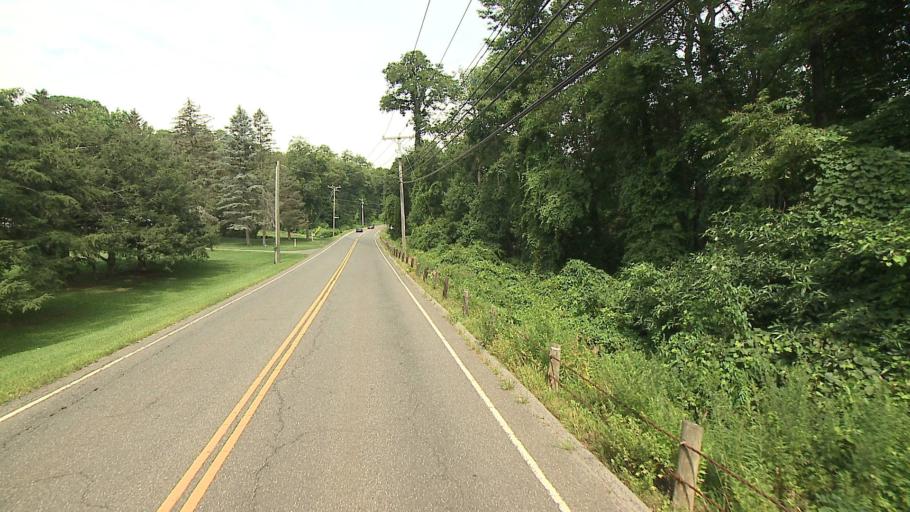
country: US
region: Connecticut
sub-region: Fairfield County
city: Sherman
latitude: 41.5540
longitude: -73.4859
